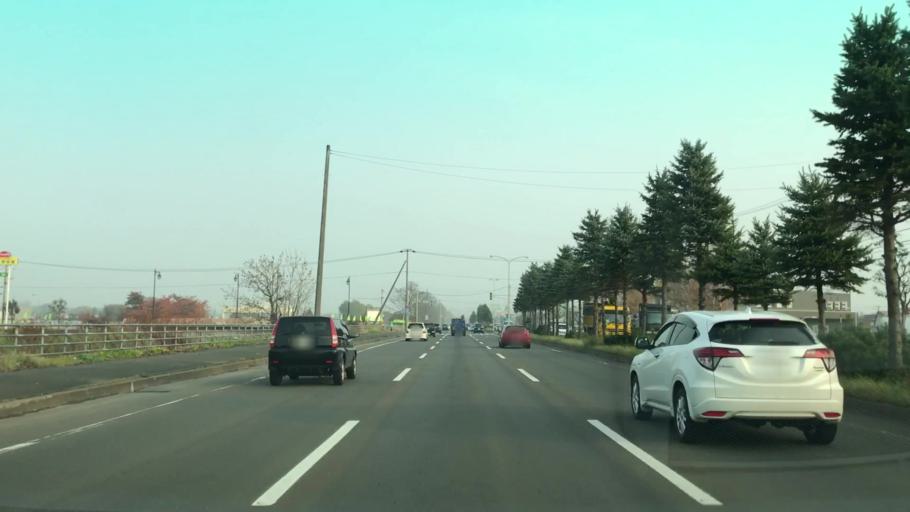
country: JP
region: Hokkaido
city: Sapporo
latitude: 43.1490
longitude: 141.3506
